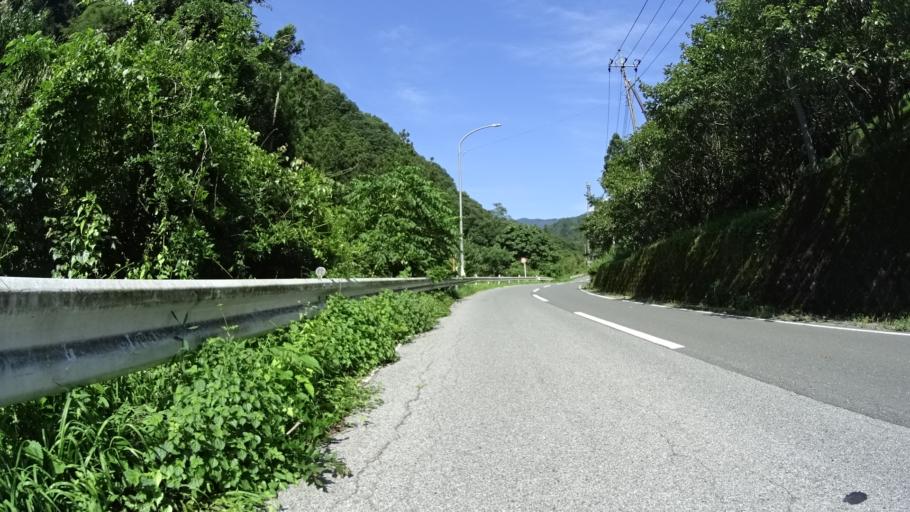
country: JP
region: Saitama
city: Chichibu
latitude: 36.0455
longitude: 138.8903
